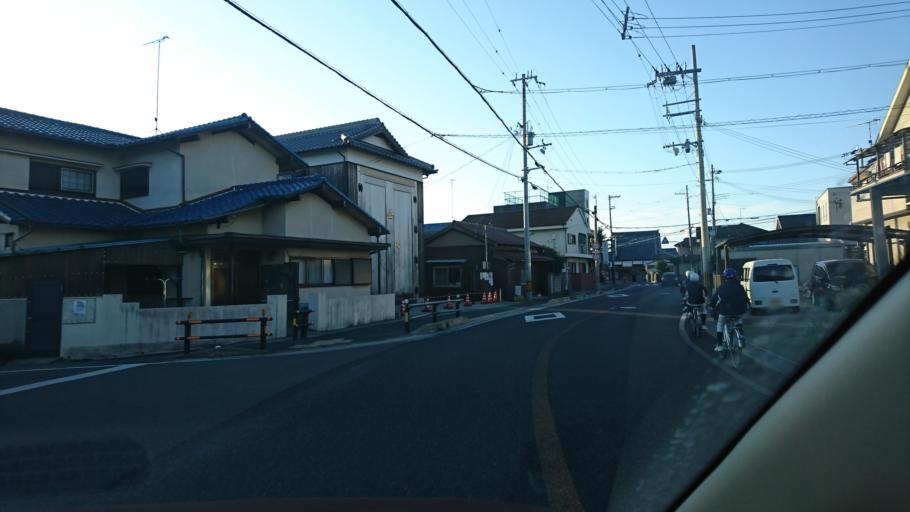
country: JP
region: Hyogo
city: Shirahamacho-usazakiminami
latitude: 34.7835
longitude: 134.7718
